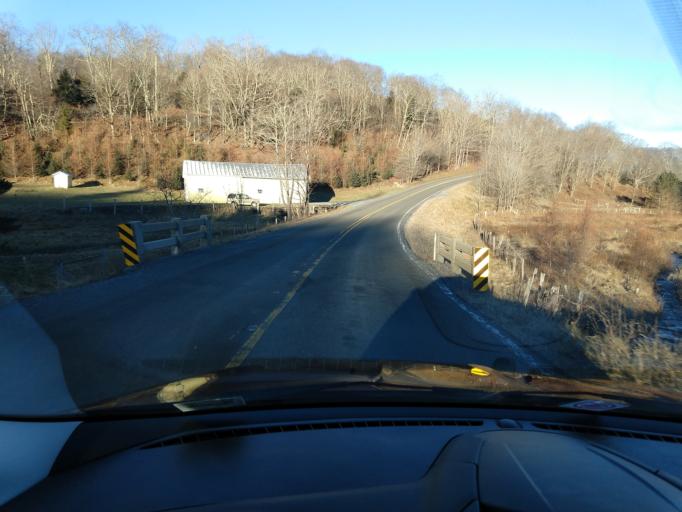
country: US
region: Virginia
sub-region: Highland County
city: Monterey
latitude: 38.4621
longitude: -79.6767
